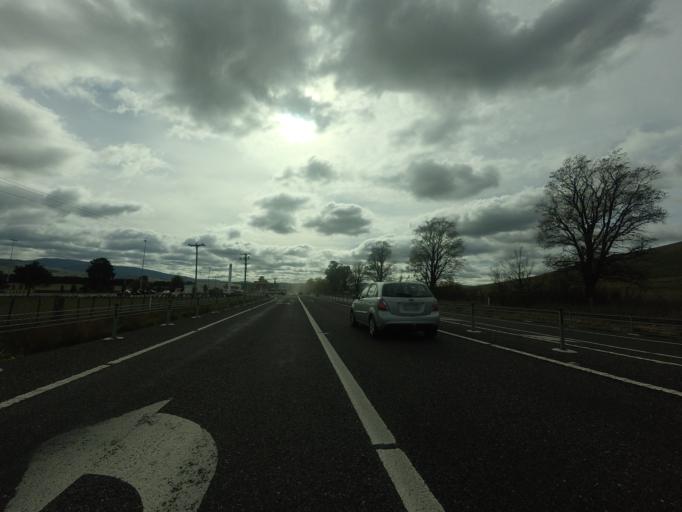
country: AU
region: Tasmania
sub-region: Brighton
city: Bridgewater
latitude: -42.5144
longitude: 147.1898
